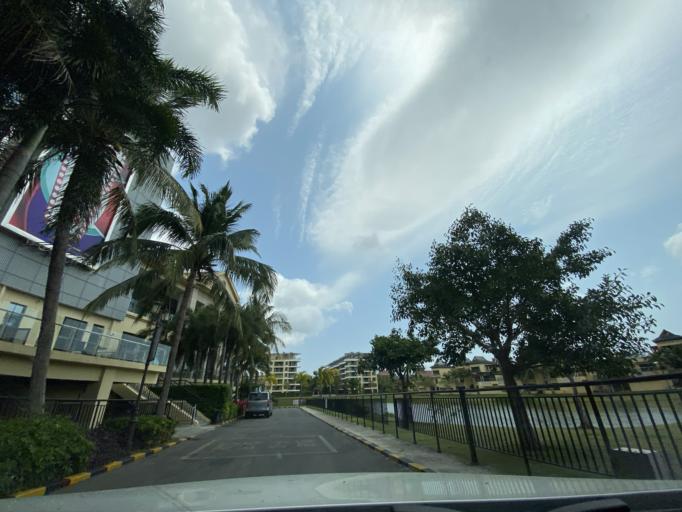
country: CN
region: Hainan
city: Tiandu
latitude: 18.2436
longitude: 109.6175
